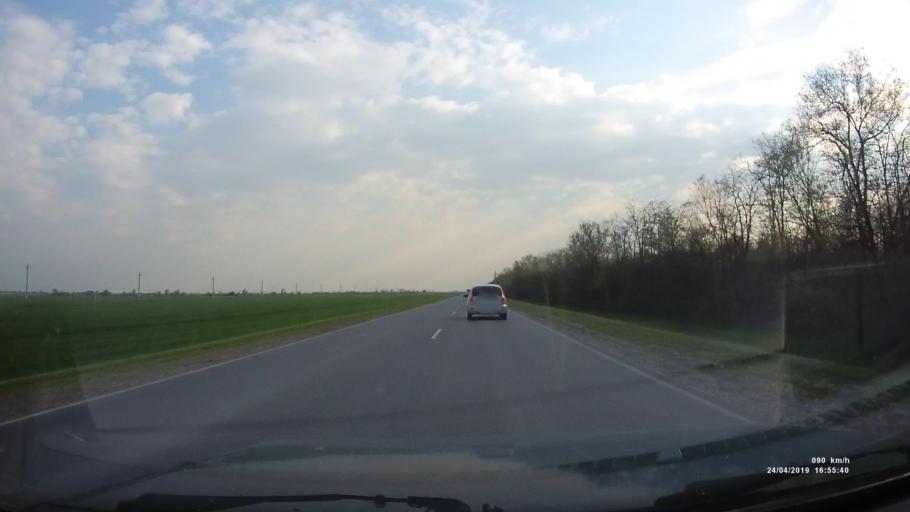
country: RU
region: Rostov
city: Proletarsk
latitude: 46.6613
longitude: 41.6856
